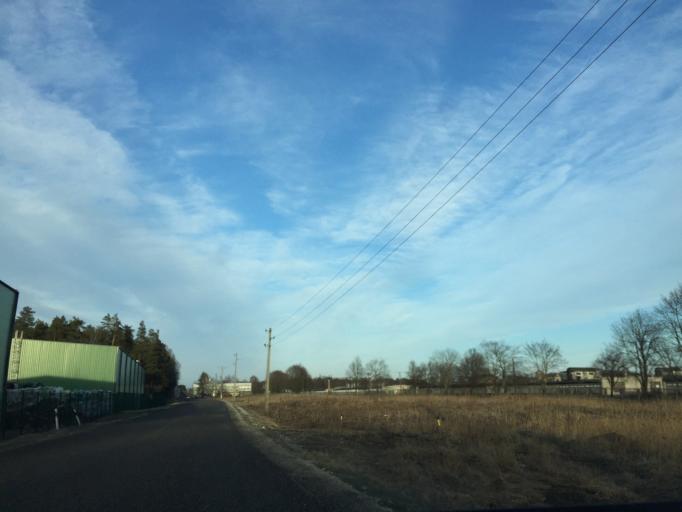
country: LV
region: Kekava
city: Kekava
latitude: 56.8250
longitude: 24.1911
